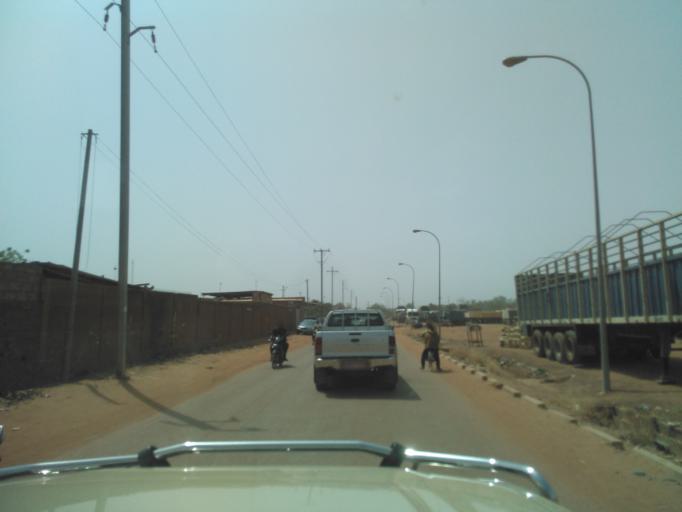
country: BF
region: Centre
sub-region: Kadiogo Province
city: Ouagadougou
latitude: 12.3946
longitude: -1.5657
